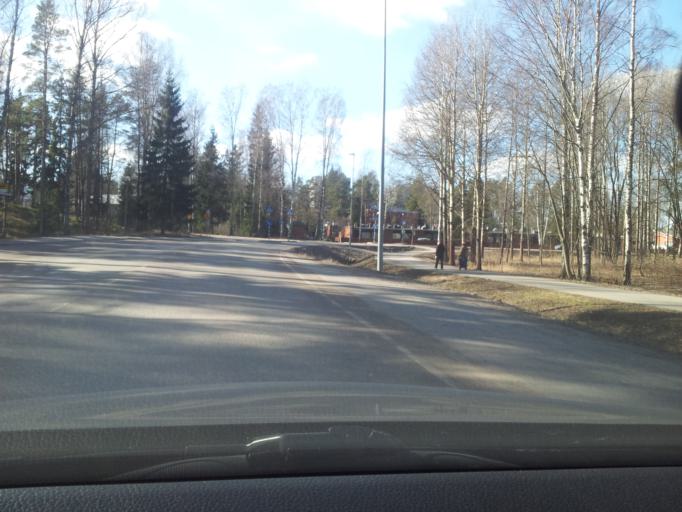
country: FI
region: Uusimaa
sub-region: Helsinki
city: Koukkuniemi
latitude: 60.1593
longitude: 24.7840
